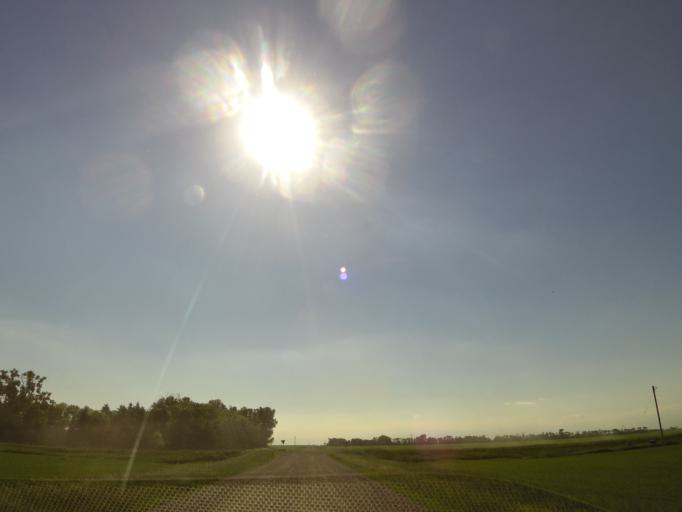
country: US
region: North Dakota
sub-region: Walsh County
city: Grafton
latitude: 48.3531
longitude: -97.2547
